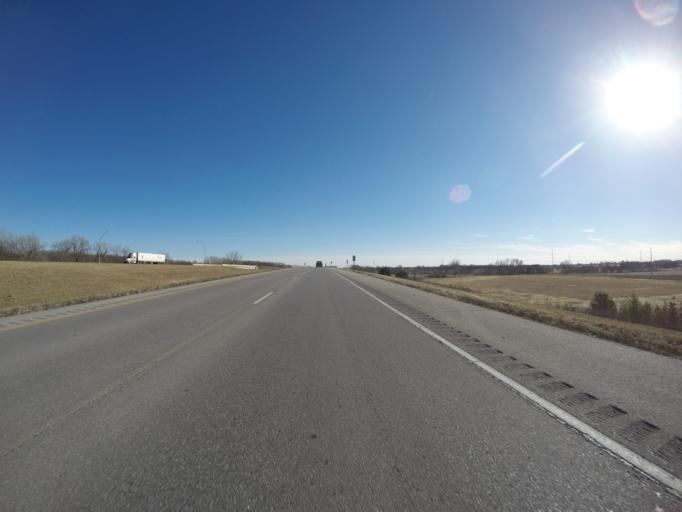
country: US
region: Nebraska
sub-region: Lancaster County
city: Lincoln
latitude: 40.7413
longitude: -96.7181
